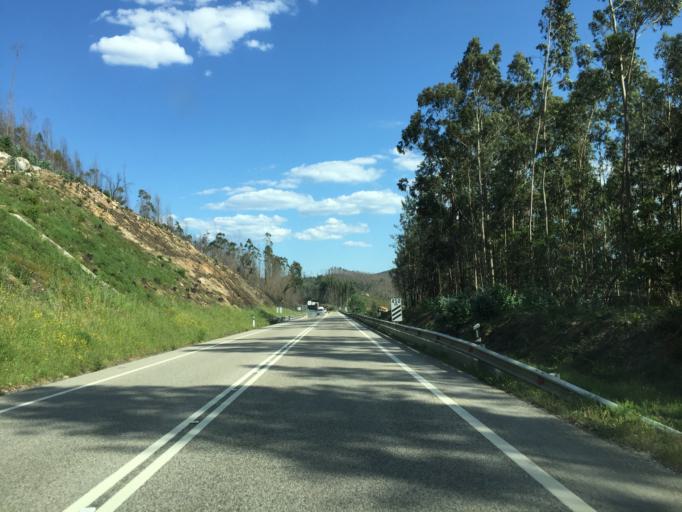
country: PT
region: Leiria
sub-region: Figueiro Dos Vinhos
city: Figueiro dos Vinhos
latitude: 39.9294
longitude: -8.3348
